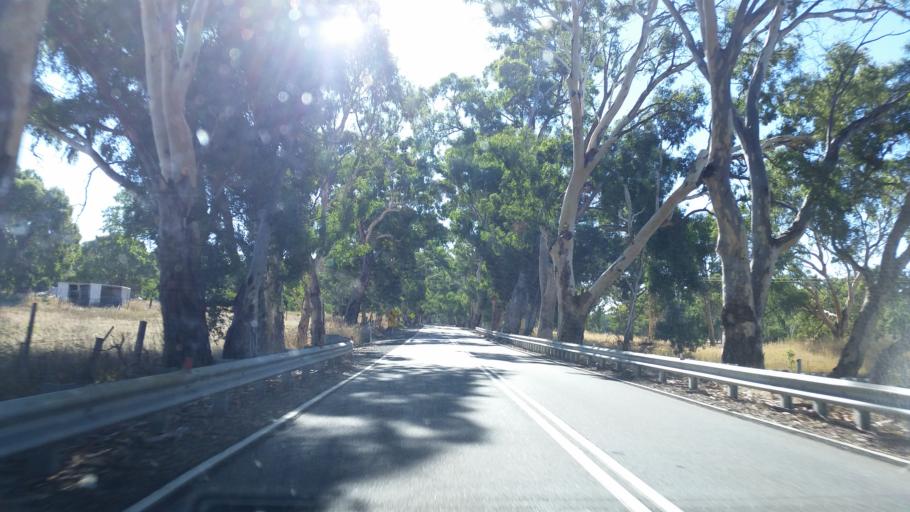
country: AU
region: South Australia
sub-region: Adelaide Hills
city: Birdwood
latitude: -34.8096
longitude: 139.0262
